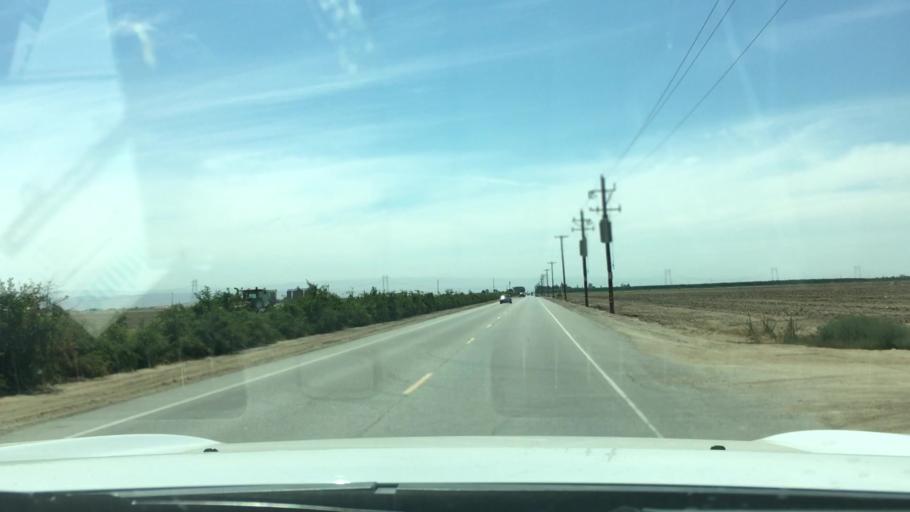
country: US
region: California
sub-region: Kern County
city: Rosedale
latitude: 35.3544
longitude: -119.2168
